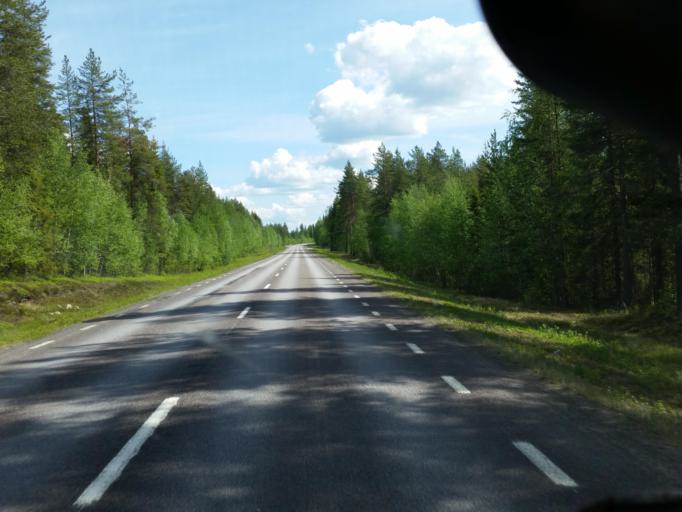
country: SE
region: Norrbotten
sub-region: Alvsbyns Kommun
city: AElvsbyn
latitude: 65.6975
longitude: 20.5220
